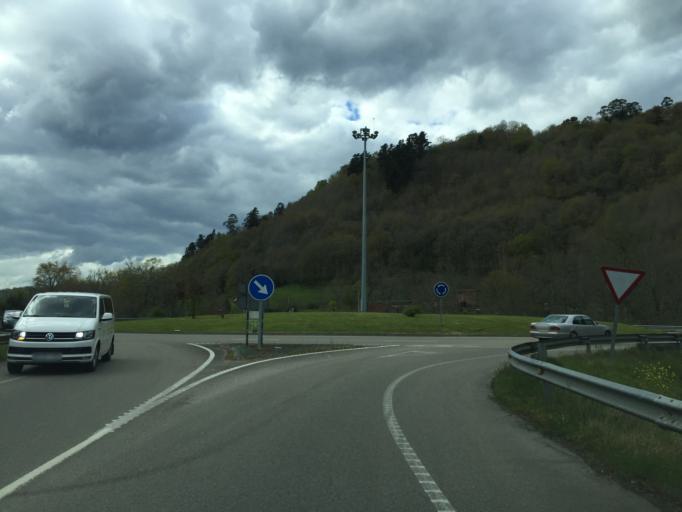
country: ES
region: Asturias
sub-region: Province of Asturias
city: Cangas de Onis
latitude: 43.3505
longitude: -5.1087
